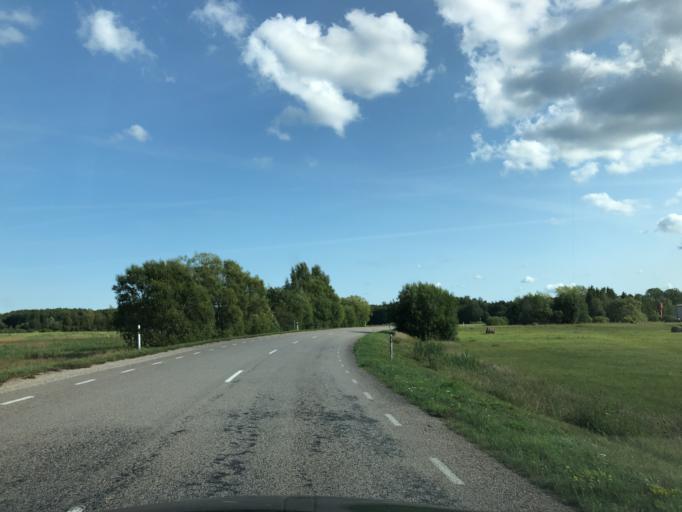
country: EE
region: Hiiumaa
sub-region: Kaerdla linn
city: Kardla
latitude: 58.7119
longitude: 22.5847
